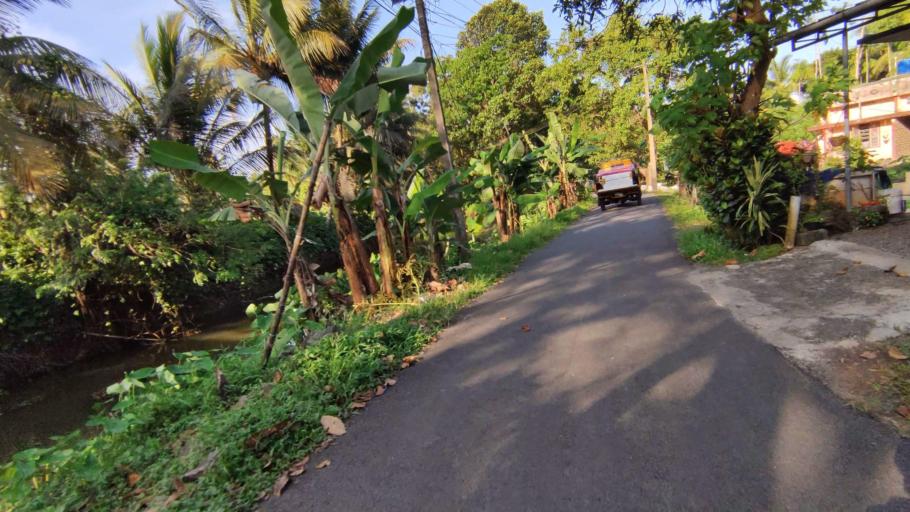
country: IN
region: Kerala
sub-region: Kottayam
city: Kottayam
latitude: 9.5958
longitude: 76.4869
